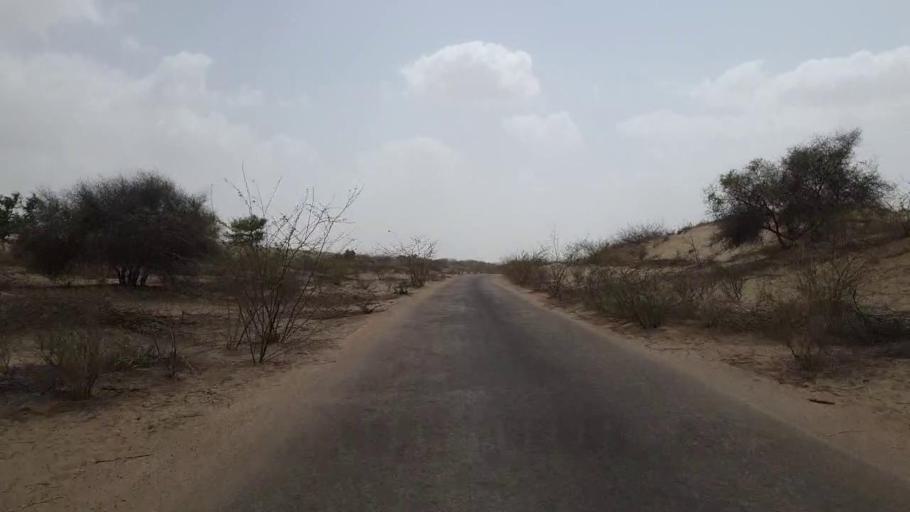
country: PK
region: Sindh
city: Diplo
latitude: 24.3712
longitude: 69.4098
